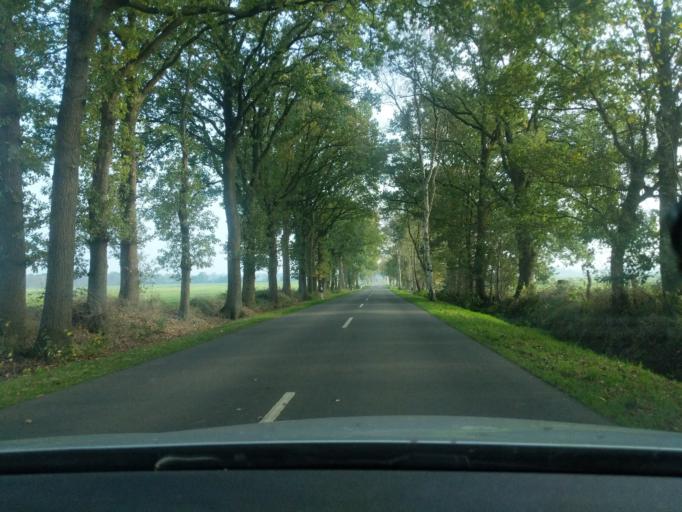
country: DE
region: Lower Saxony
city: Stinstedt
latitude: 53.6567
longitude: 8.9797
